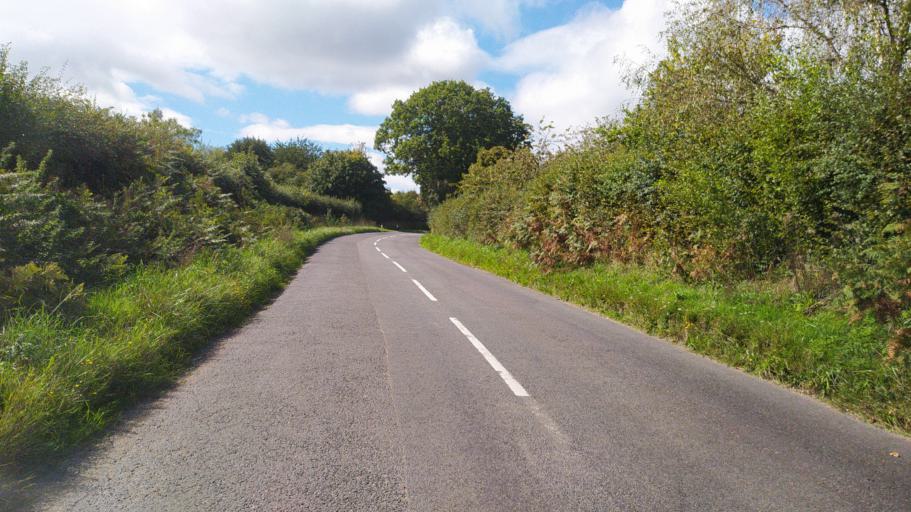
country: GB
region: England
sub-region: Hampshire
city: Romsey
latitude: 51.0136
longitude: -1.5323
